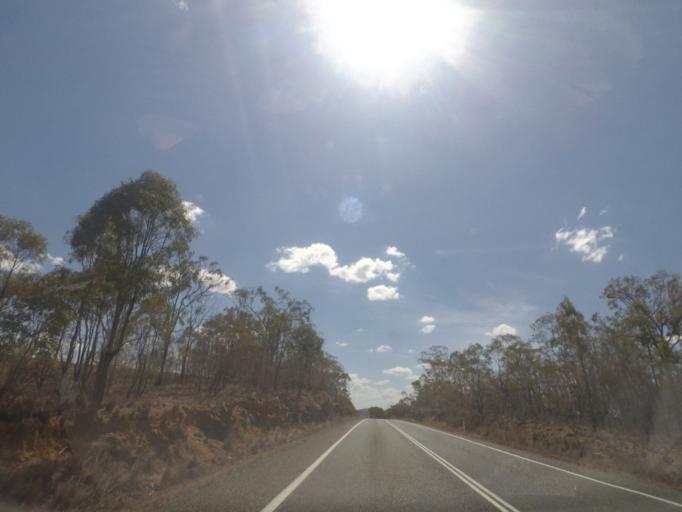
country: AU
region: Queensland
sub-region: Southern Downs
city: Warwick
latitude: -28.2055
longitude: 151.5762
